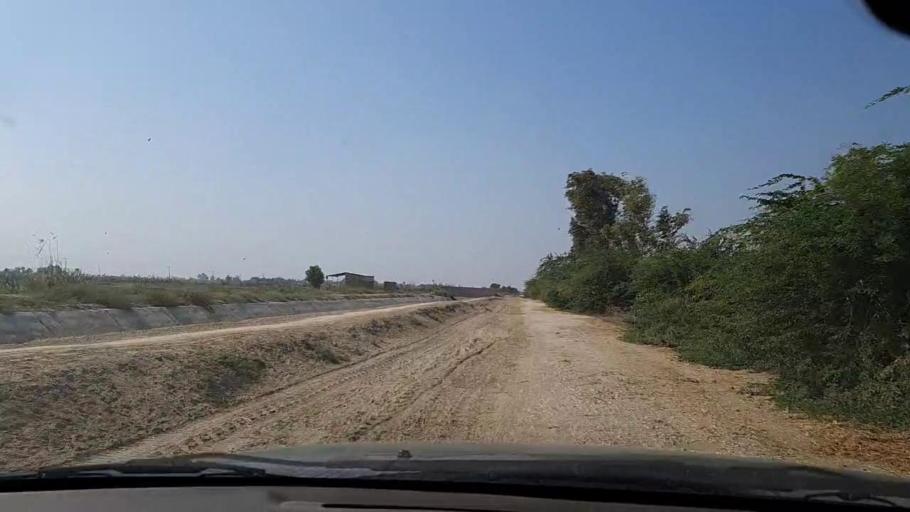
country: PK
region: Sindh
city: Chuhar Jamali
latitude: 24.4276
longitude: 67.8083
